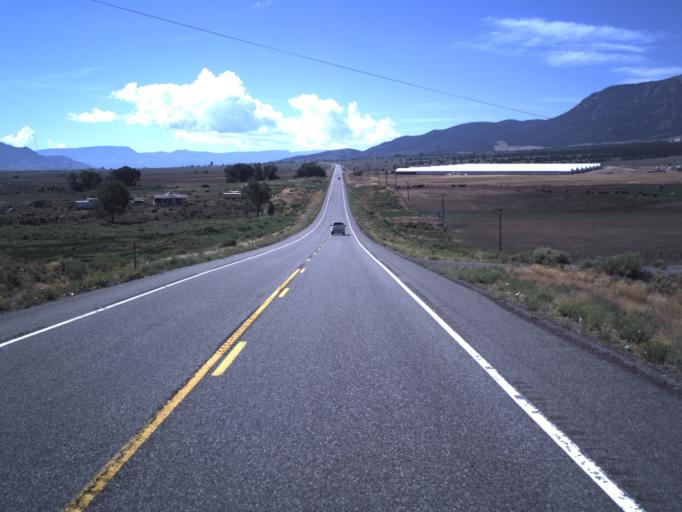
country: US
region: Utah
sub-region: Piute County
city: Junction
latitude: 38.4134
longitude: -112.2314
